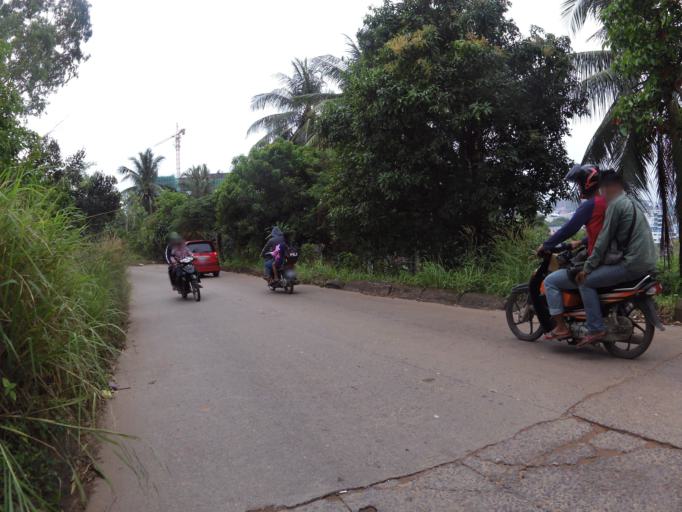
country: KH
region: Preah Sihanouk
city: Sihanoukville
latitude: 10.6277
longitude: 103.5260
